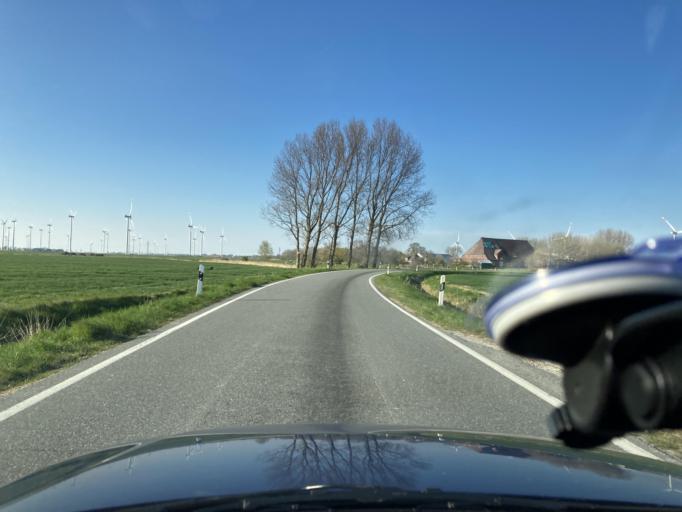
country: DE
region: Schleswig-Holstein
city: Lieth
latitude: 54.1658
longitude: 9.0326
